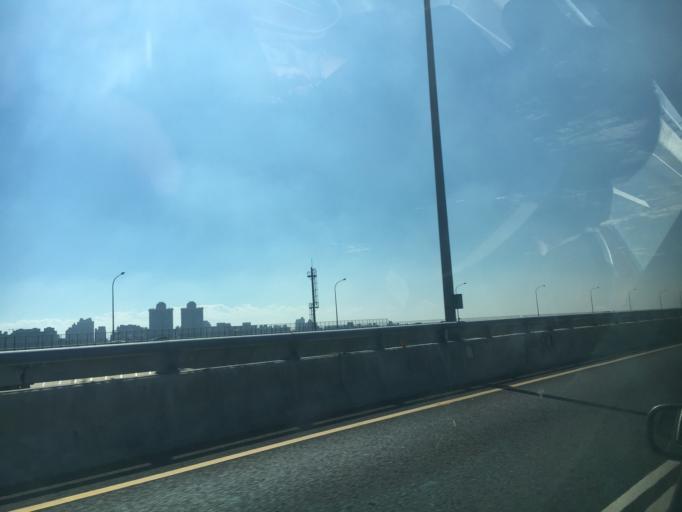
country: TW
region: Taiwan
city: Taoyuan City
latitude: 25.0363
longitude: 121.2946
